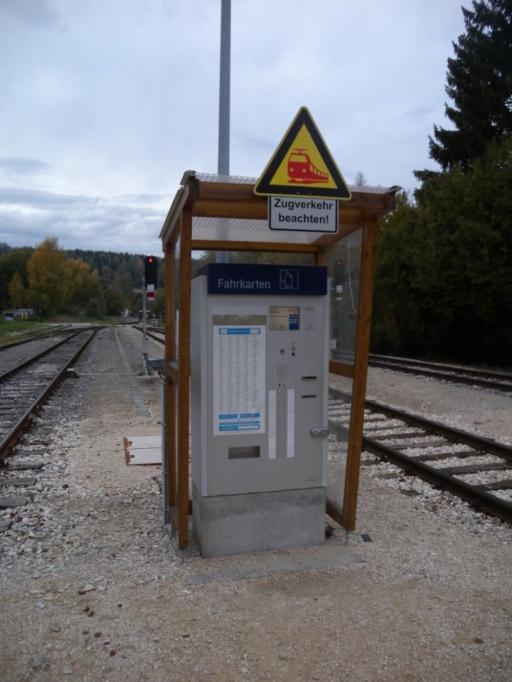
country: DE
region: Baden-Wuerttemberg
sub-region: Tuebingen Region
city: Sigmaringen
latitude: 48.0999
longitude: 9.2354
